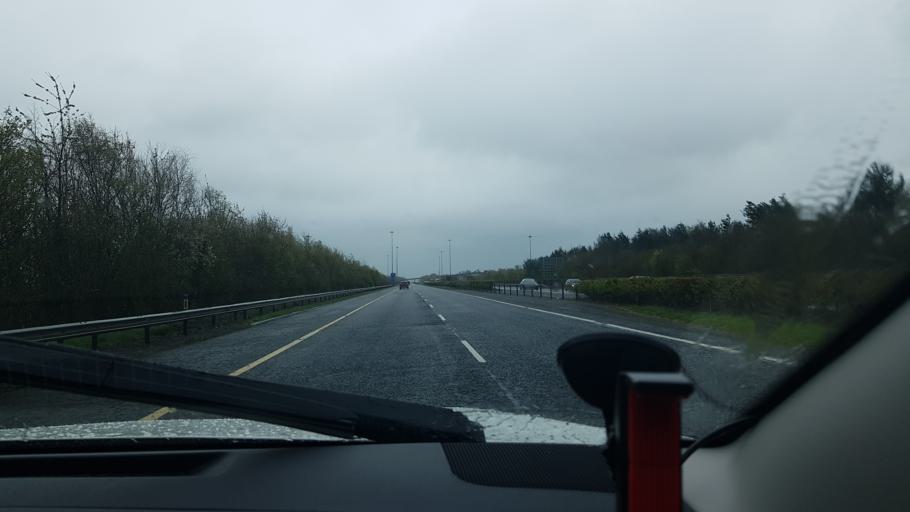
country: IE
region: Leinster
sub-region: Lu
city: Dunleer
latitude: 53.8417
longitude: -6.4181
